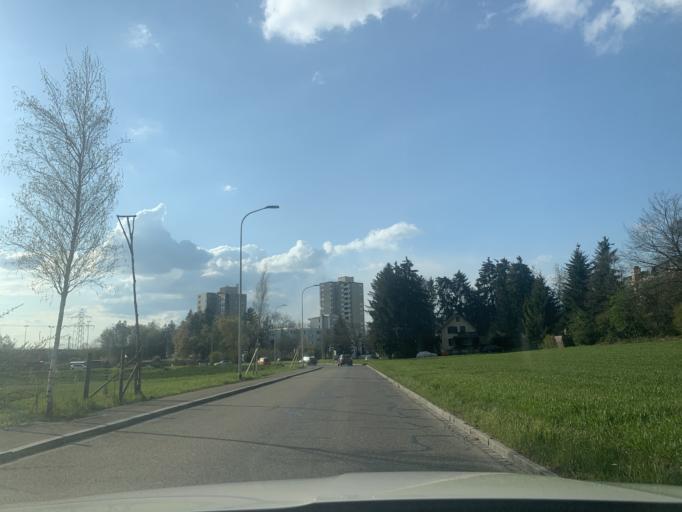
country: CH
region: Zurich
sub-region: Bezirk Buelach
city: Grossacker/Opfikon
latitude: 47.4222
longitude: 8.5780
